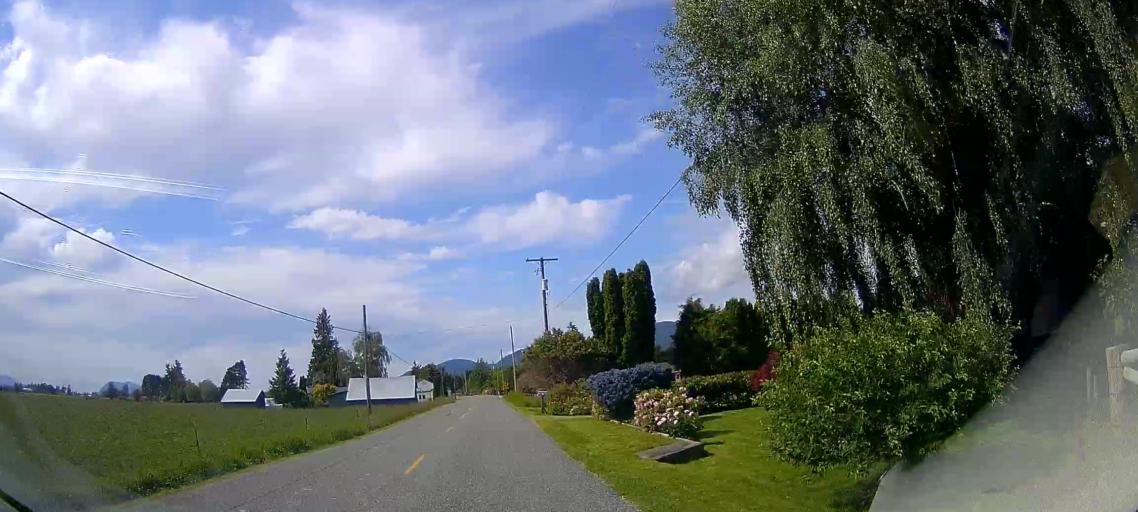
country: US
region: Washington
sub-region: Skagit County
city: Burlington
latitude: 48.5426
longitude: -122.3918
